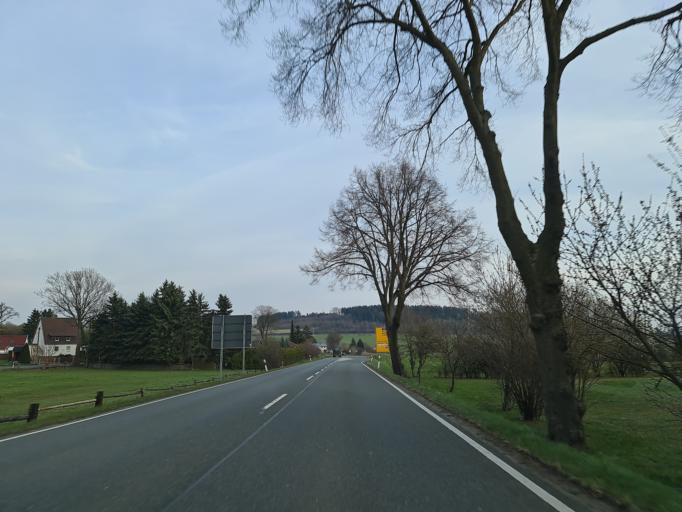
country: DE
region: Saxony
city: Oelsnitz
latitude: 50.4567
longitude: 12.1606
